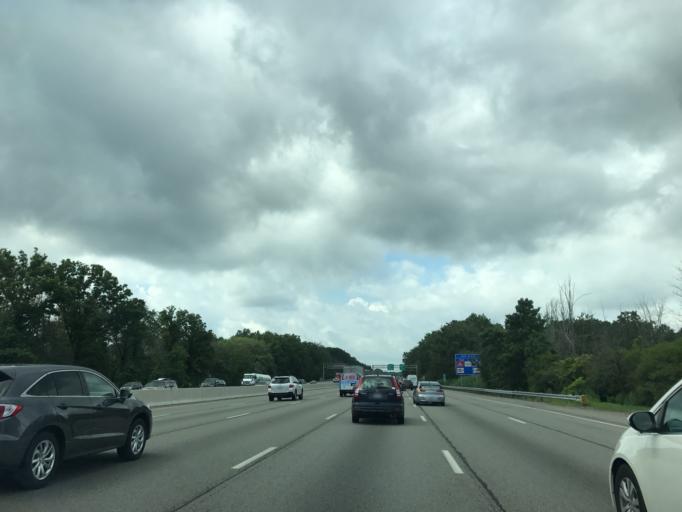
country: US
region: New Jersey
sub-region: Morris County
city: Parsippany
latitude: 40.8443
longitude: -74.4304
